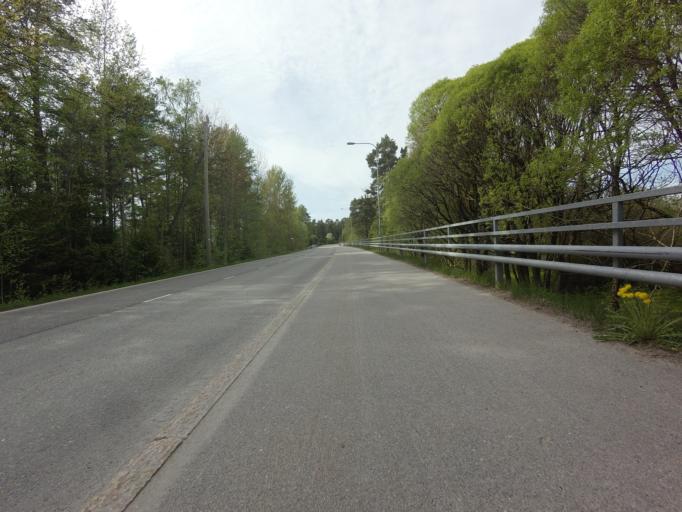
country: FI
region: Uusimaa
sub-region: Helsinki
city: Koukkuniemi
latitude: 60.1215
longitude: 24.7163
